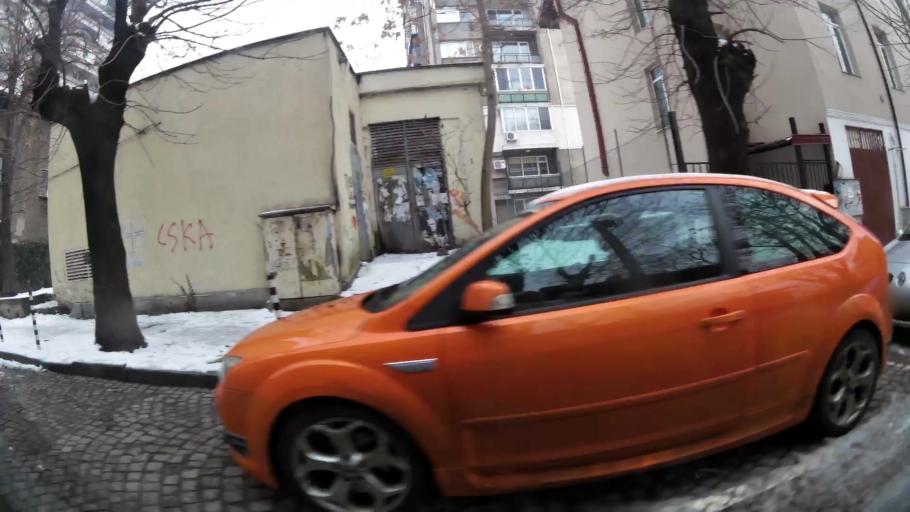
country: BG
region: Sofia-Capital
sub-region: Stolichna Obshtina
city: Sofia
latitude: 42.7068
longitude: 23.3219
